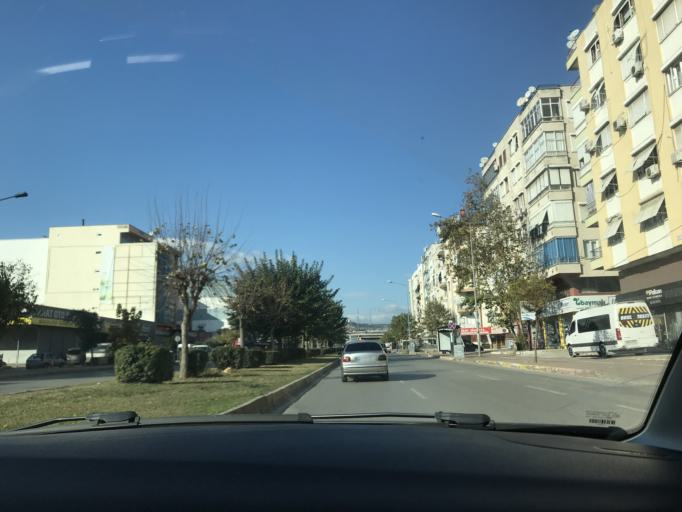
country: TR
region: Antalya
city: Antalya
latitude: 36.9085
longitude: 30.6990
